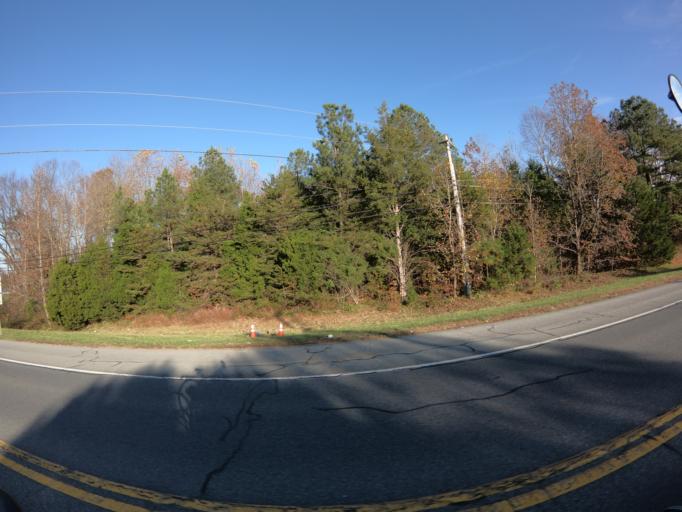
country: US
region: Maryland
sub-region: Saint Mary's County
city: Leonardtown
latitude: 38.3157
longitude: -76.6689
